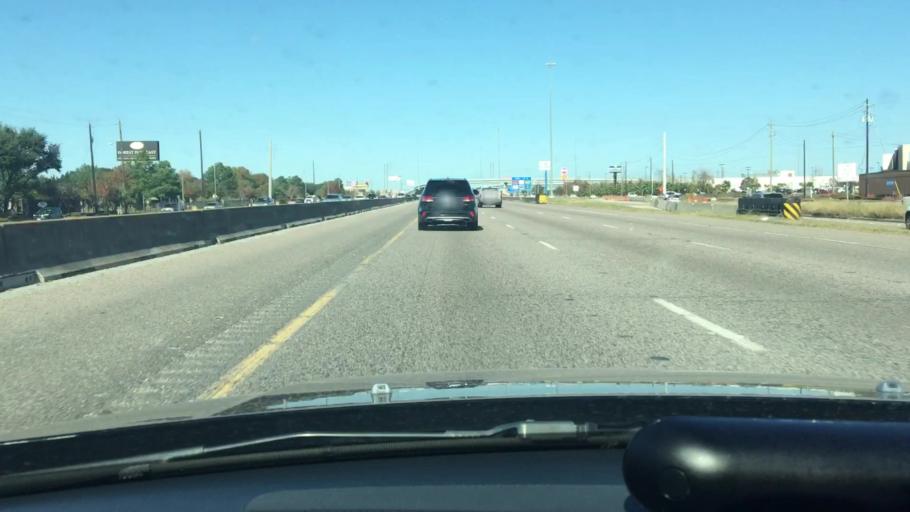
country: US
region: Texas
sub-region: Harris County
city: Webster
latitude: 29.5143
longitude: -95.1208
